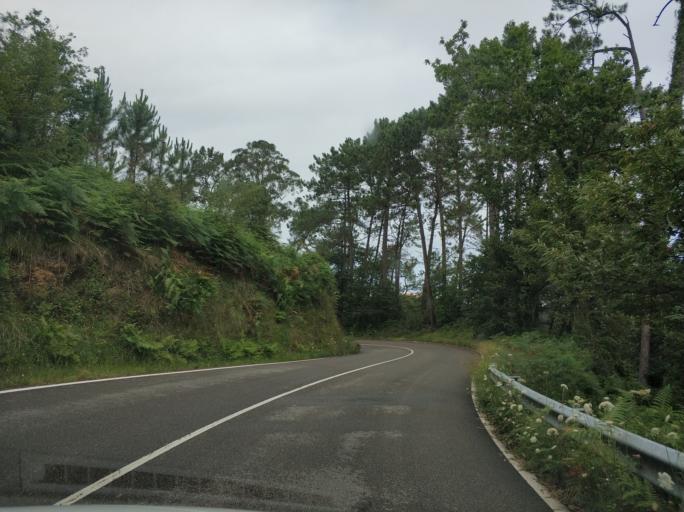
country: ES
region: Asturias
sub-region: Province of Asturias
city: Cudillero
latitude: 43.5583
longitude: -6.2907
